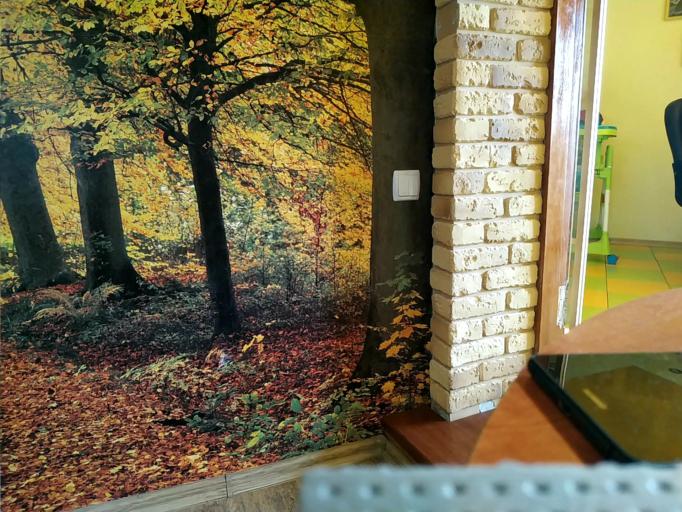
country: RU
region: Tverskaya
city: Zubtsov
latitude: 56.2176
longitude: 34.5330
